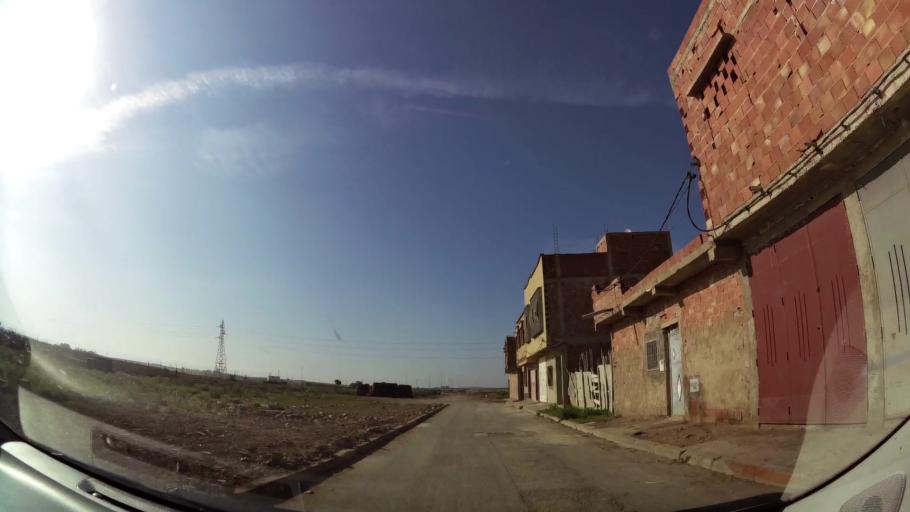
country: MA
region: Oriental
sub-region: Oujda-Angad
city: Oujda
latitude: 34.7252
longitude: -1.8930
